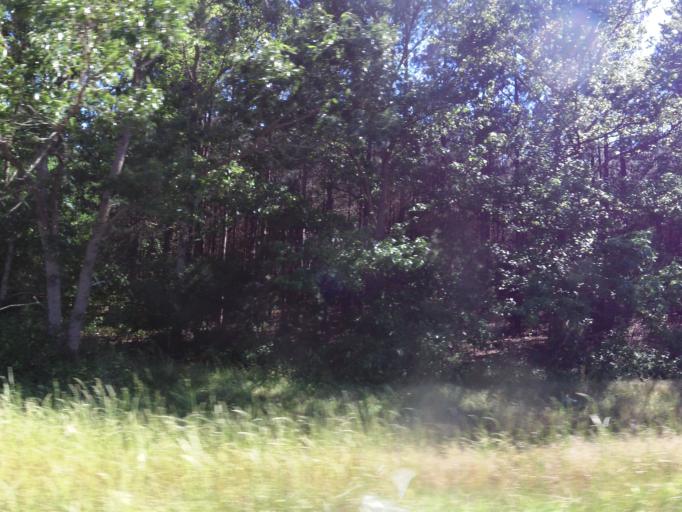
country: US
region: South Carolina
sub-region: Bamberg County
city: Denmark
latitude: 33.3384
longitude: -81.1722
